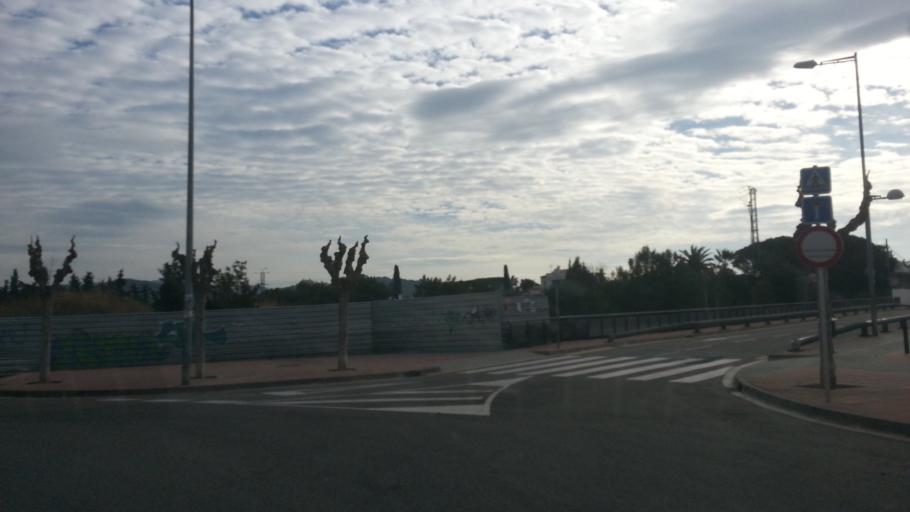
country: ES
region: Catalonia
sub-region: Provincia de Barcelona
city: Sant Pere de Ribes
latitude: 41.2552
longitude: 1.7753
